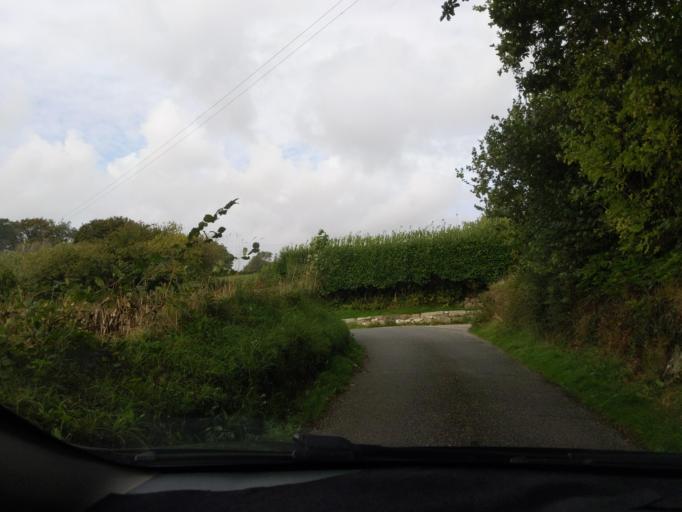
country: GB
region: England
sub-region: Cornwall
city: Lostwithiel
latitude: 50.4010
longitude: -4.6945
